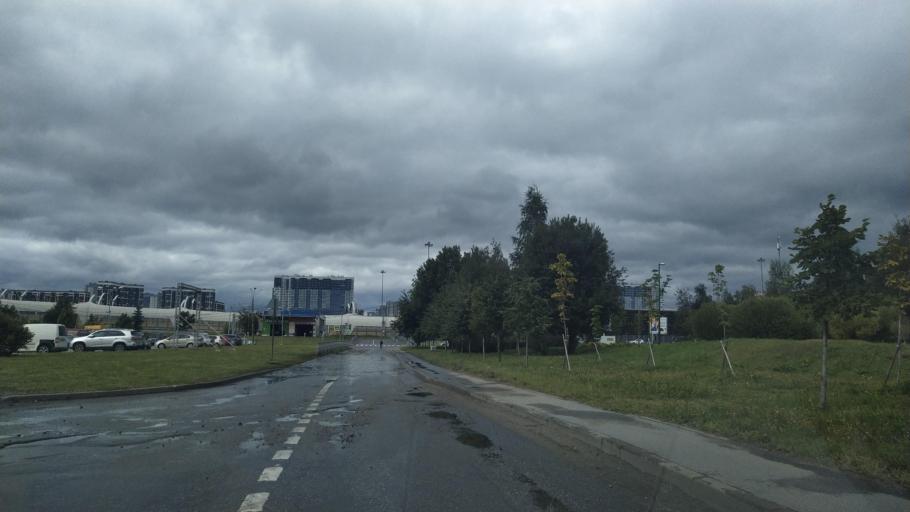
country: RU
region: St.-Petersburg
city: Staraya Derevnya
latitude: 59.9995
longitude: 30.2368
